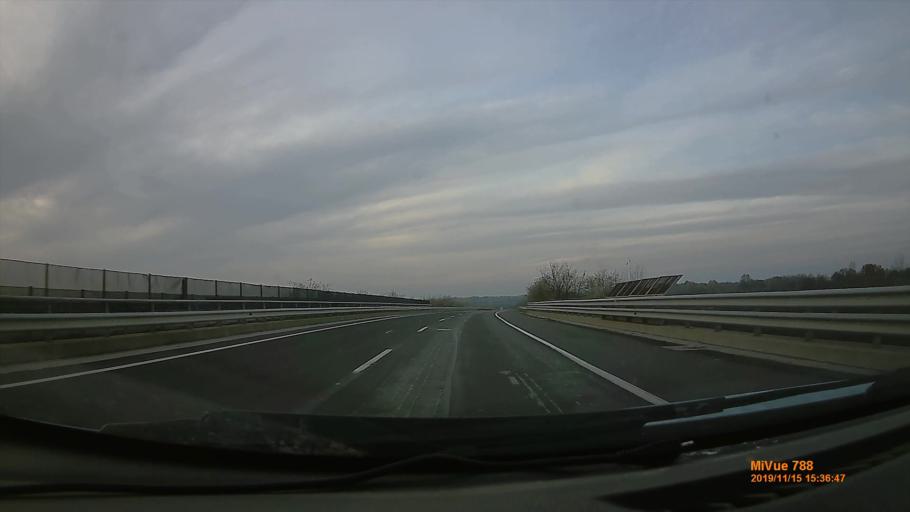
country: HU
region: Bekes
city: Gyula
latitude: 46.6593
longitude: 21.2072
